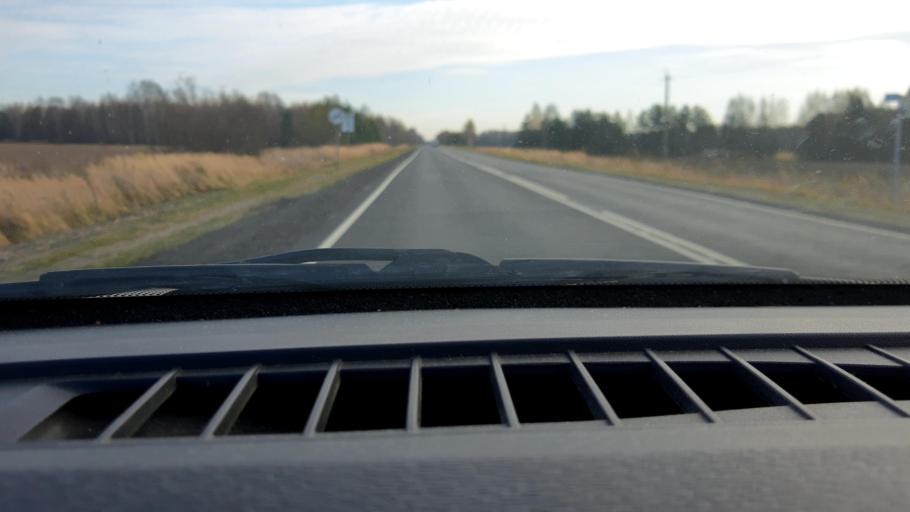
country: RU
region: Nizjnij Novgorod
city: Novaya Balakhna
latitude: 56.5957
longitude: 43.6472
